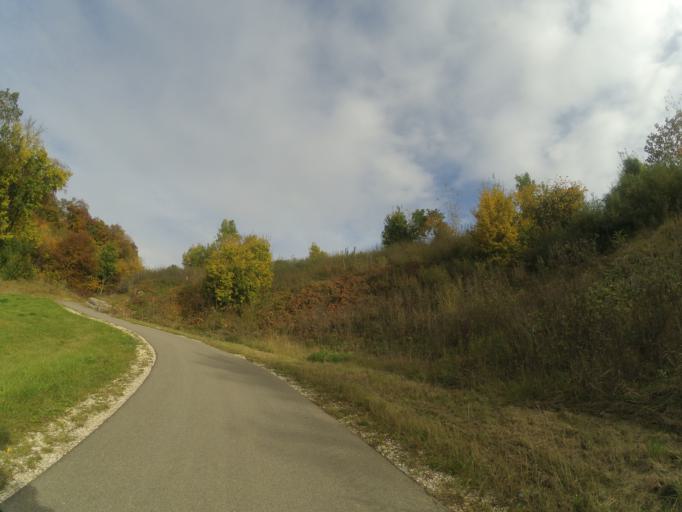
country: DE
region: Baden-Wuerttemberg
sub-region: Tuebingen Region
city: Lonsee
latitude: 48.5489
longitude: 9.9206
